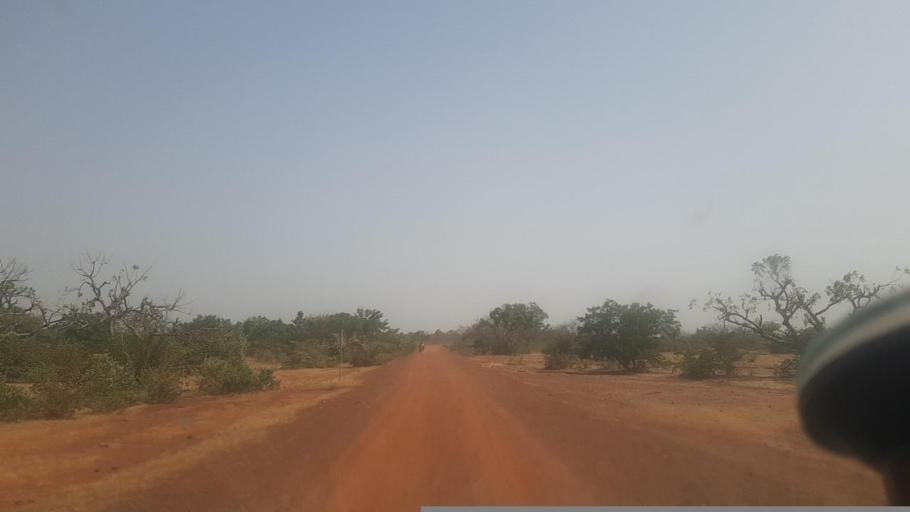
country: ML
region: Segou
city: Segou
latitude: 12.9311
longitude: -6.2836
